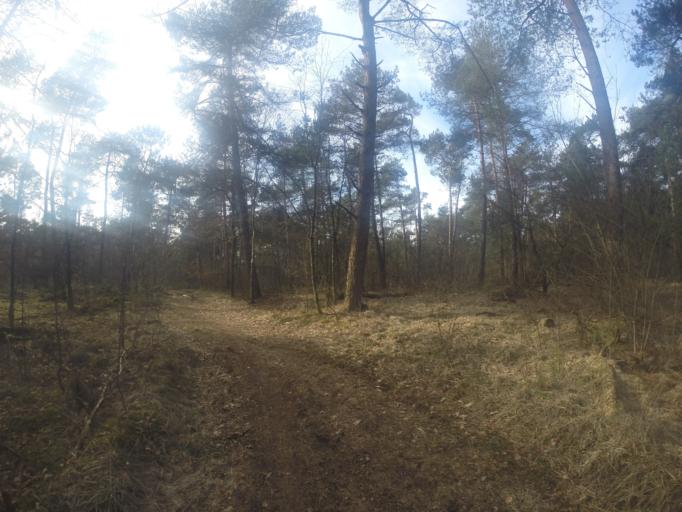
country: NL
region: Gelderland
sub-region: Gemeente Lochem
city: Lochem
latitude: 52.1343
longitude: 6.3563
